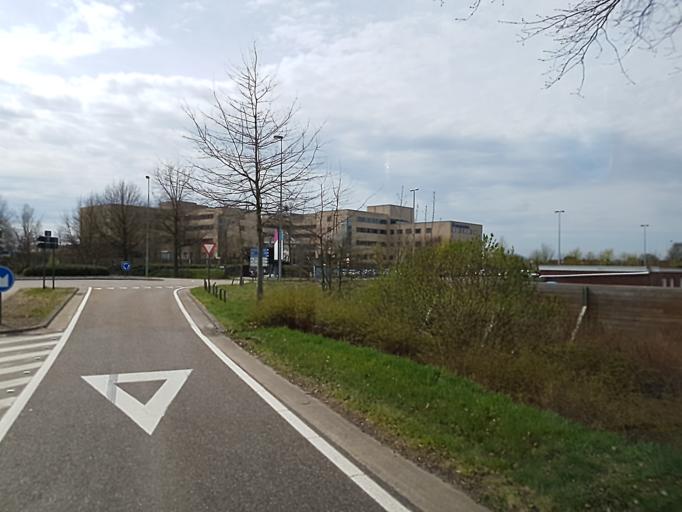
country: BE
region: Flanders
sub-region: Provincie Limburg
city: Overpelt
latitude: 51.2135
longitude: 5.4196
